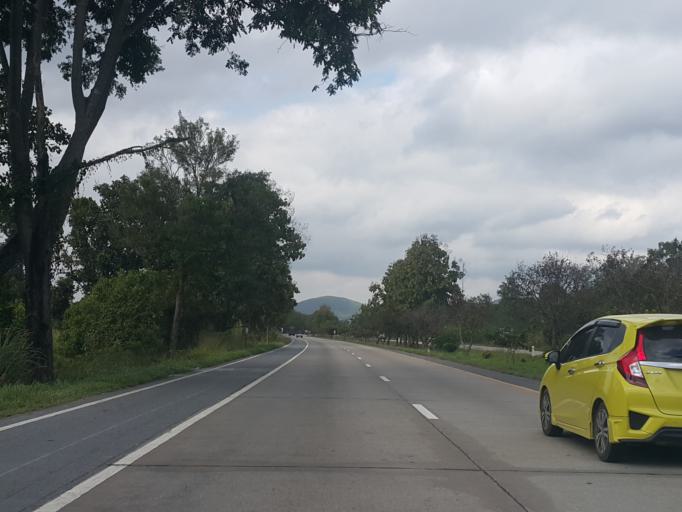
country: TH
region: Lamphun
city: Mae Tha
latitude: 18.4562
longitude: 99.1910
